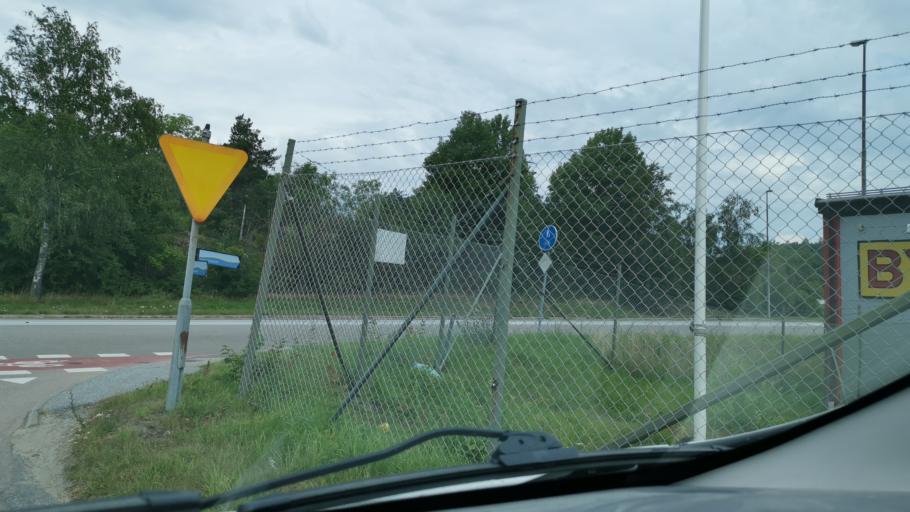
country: SE
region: Vaestra Goetaland
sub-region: Uddevalla Kommun
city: Uddevalla
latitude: 58.3523
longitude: 11.9589
